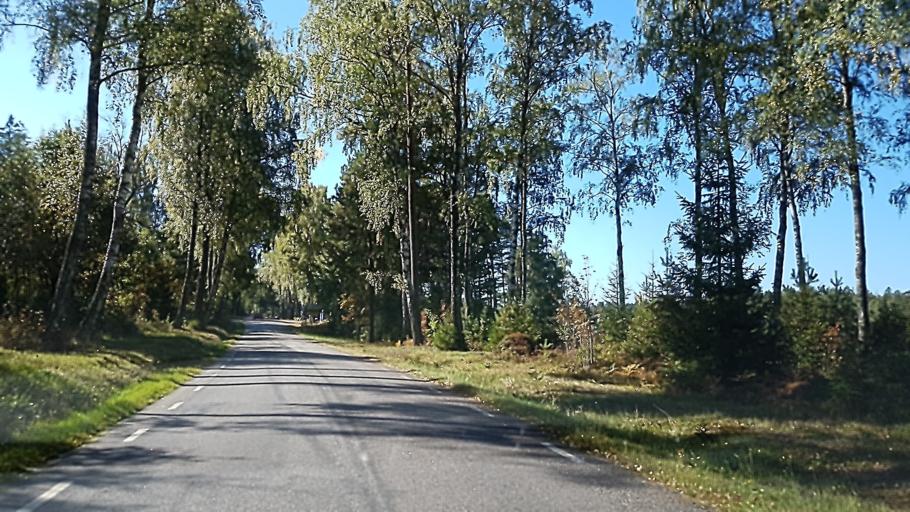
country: SE
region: Kronoberg
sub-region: Ljungby Kommun
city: Ljungby
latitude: 56.8016
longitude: 14.0329
